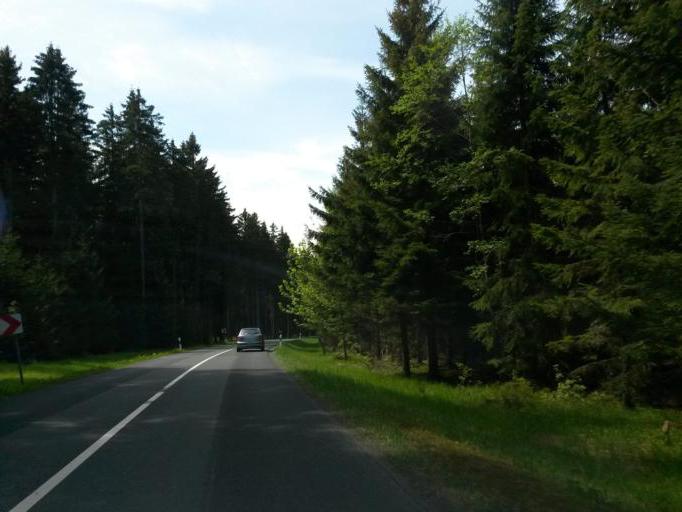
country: DE
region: Saxony
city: Zwota
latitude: 50.3641
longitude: 12.4028
